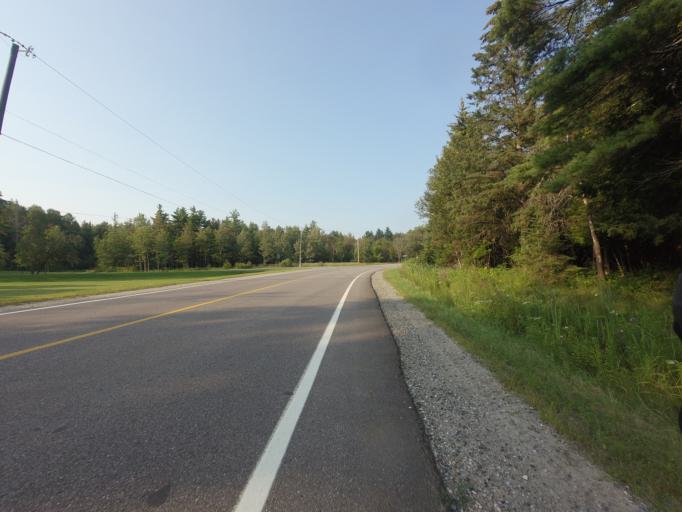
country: CA
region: Ontario
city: Perth
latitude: 44.9465
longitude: -76.6828
